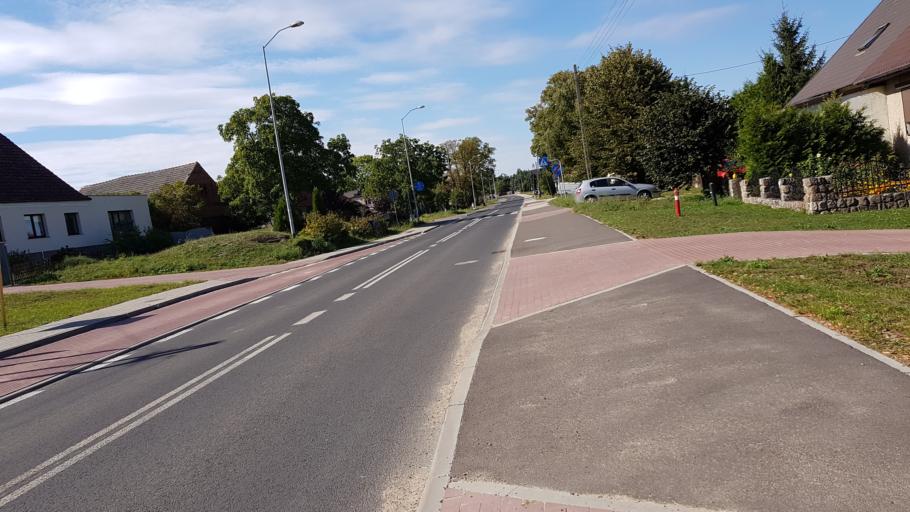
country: PL
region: West Pomeranian Voivodeship
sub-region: Powiat policki
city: Przeclaw
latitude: 53.3500
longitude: 14.4756
